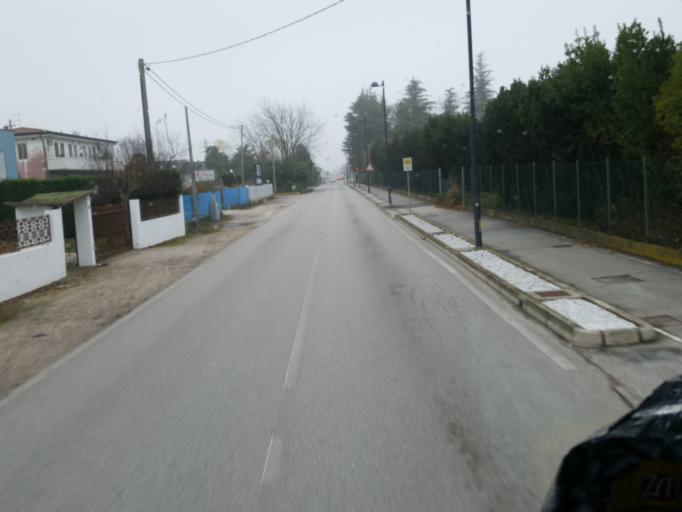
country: IT
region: Veneto
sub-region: Provincia di Padova
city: Campodarsego
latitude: 45.4812
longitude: 11.9120
